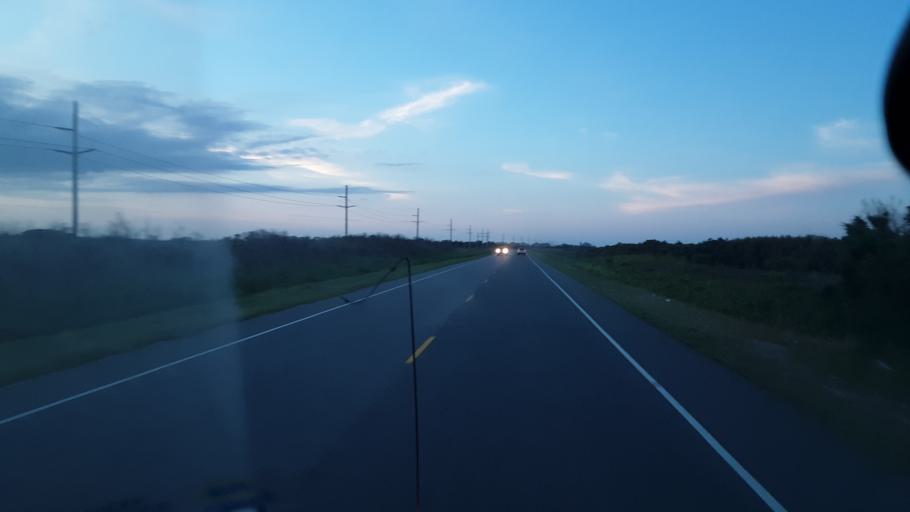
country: US
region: North Carolina
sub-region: Dare County
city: Buxton
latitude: 35.3095
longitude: -75.5117
